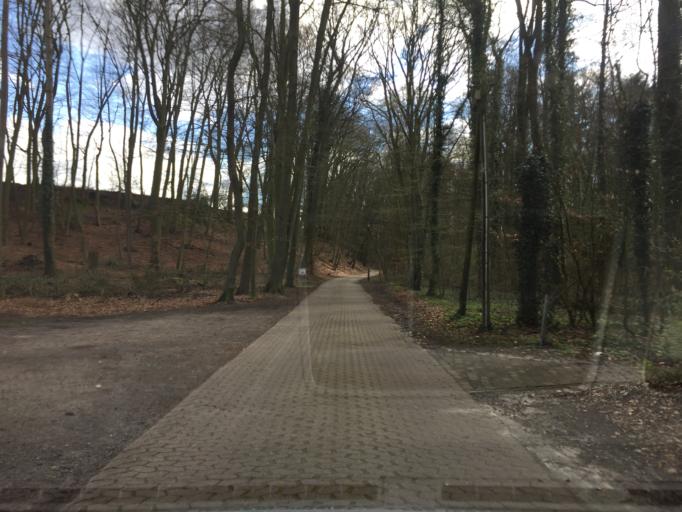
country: DE
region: Lower Saxony
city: Bruchhausen-Vilsen
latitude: 52.8042
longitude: 8.9956
